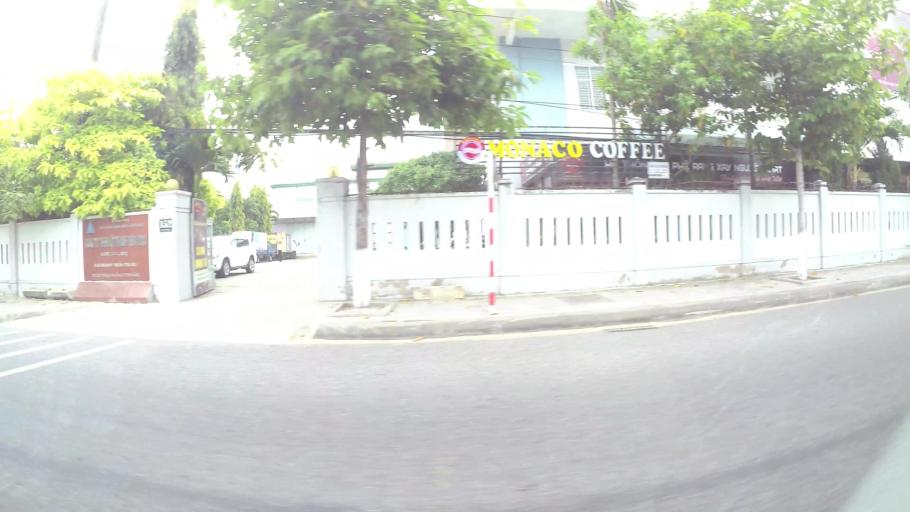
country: VN
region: Da Nang
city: Da Nang
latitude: 16.0517
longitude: 108.2046
